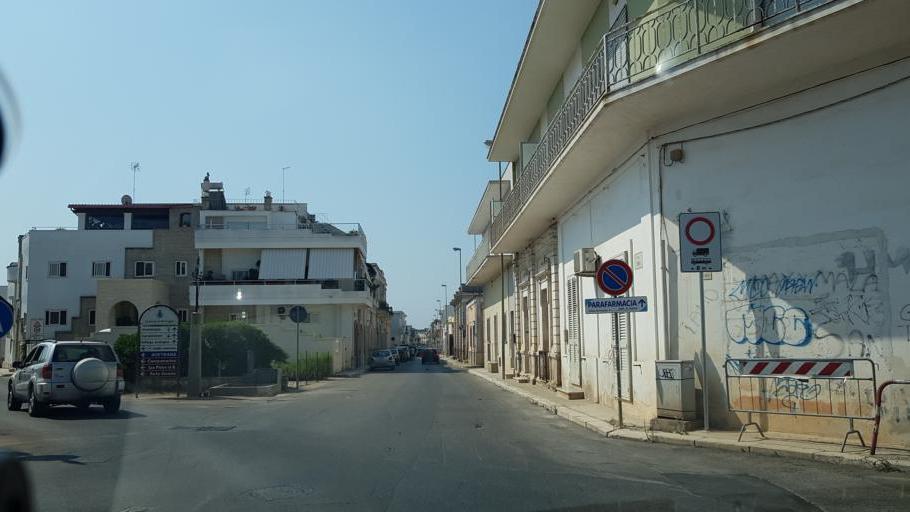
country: IT
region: Apulia
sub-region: Provincia di Taranto
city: Maruggio
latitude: 40.3261
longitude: 17.5730
